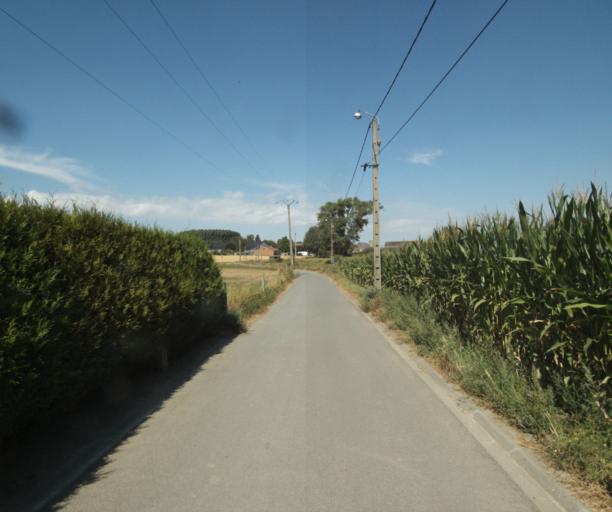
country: FR
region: Nord-Pas-de-Calais
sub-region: Departement du Nord
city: Neuville-en-Ferrain
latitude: 50.7733
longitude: 3.1561
